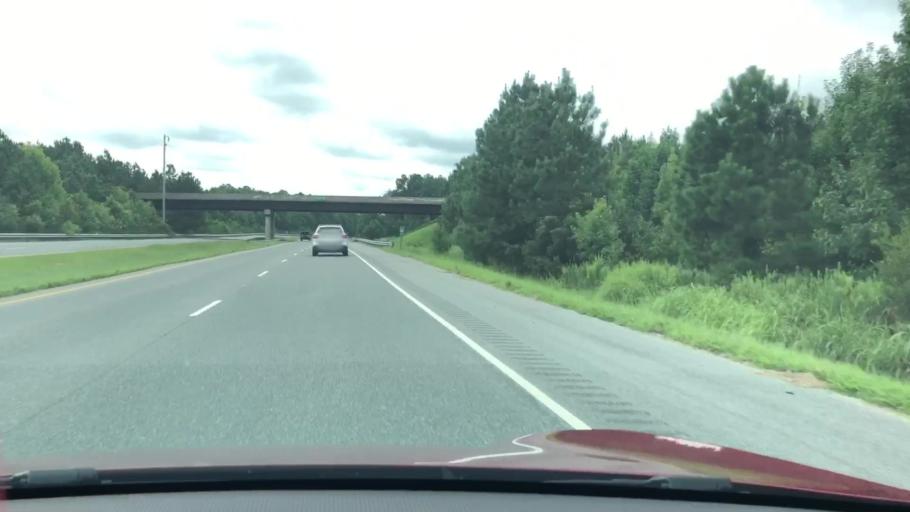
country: US
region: North Carolina
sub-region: Currituck County
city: Moyock
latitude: 36.6335
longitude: -76.2165
